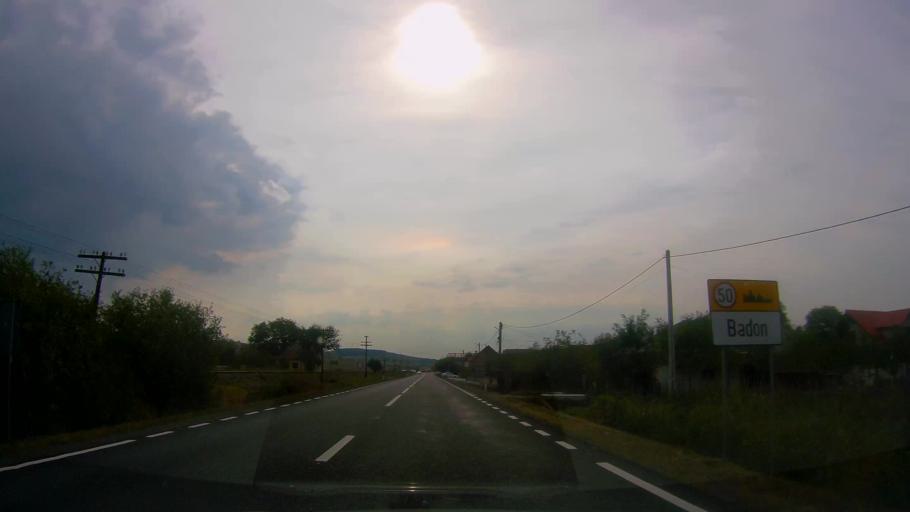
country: RO
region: Salaj
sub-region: Comuna Hereclean
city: Hereclean
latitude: 47.2559
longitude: 22.9765
